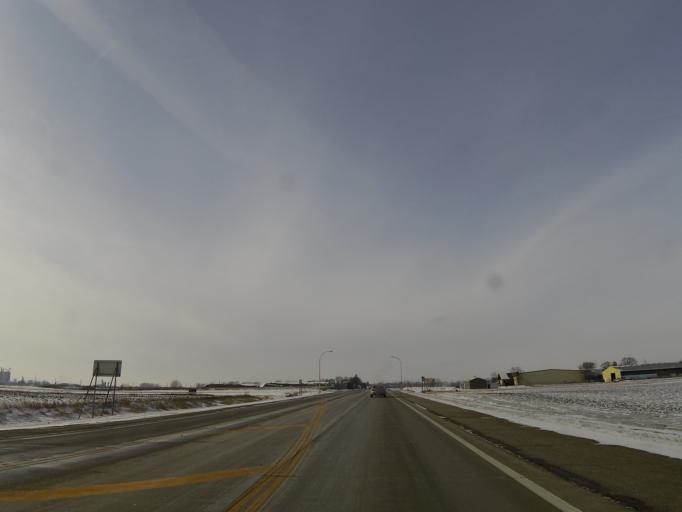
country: US
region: Minnesota
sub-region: McLeod County
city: Hutchinson
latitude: 44.8962
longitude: -94.3310
